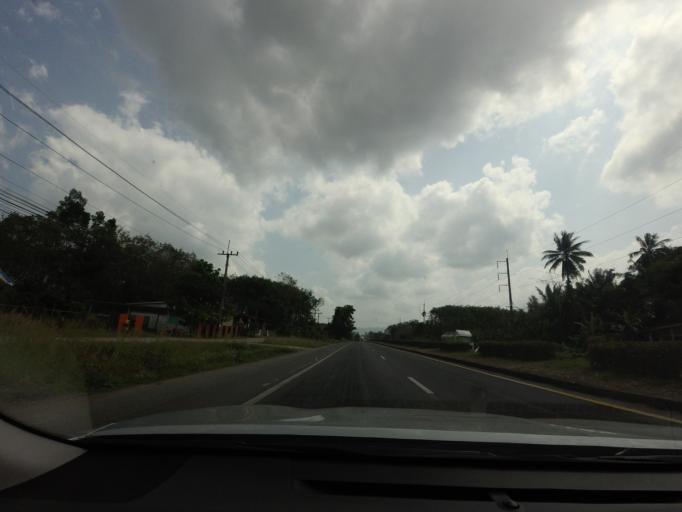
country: TH
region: Phangnga
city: Thap Put
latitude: 8.5089
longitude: 98.6575
